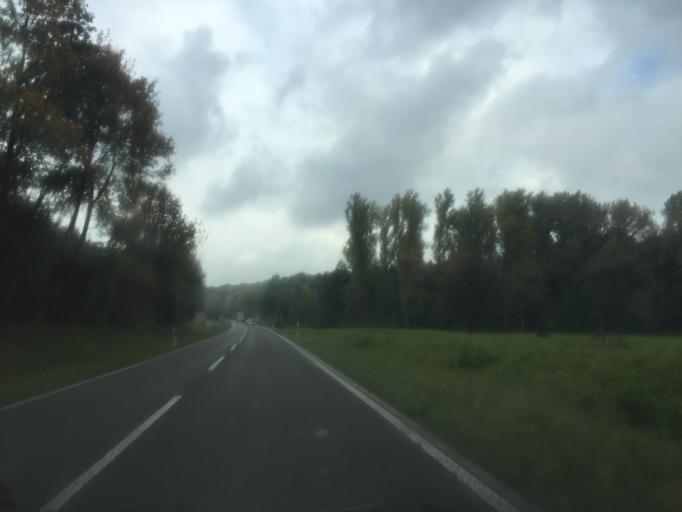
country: DE
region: Baden-Wuerttemberg
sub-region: Karlsruhe Region
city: Bretten
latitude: 49.0585
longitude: 8.7162
